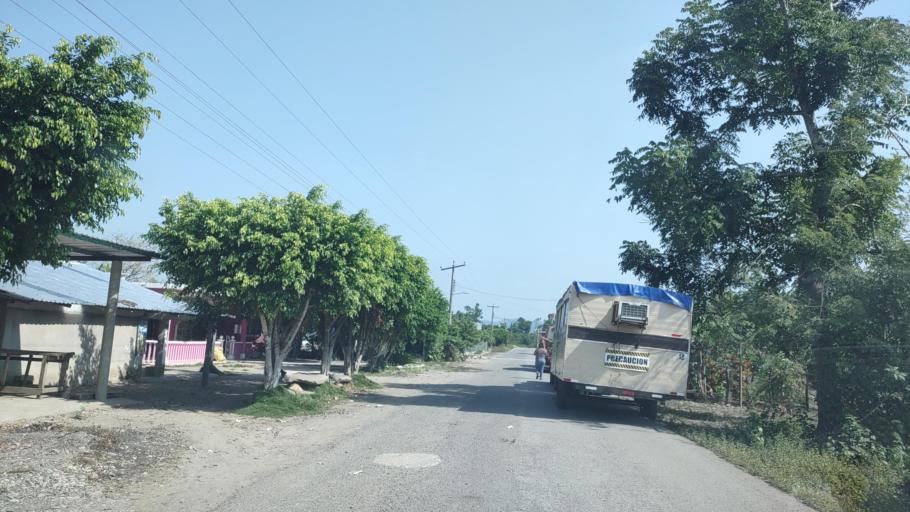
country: MX
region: Puebla
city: Espinal
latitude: 20.2551
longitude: -97.3297
